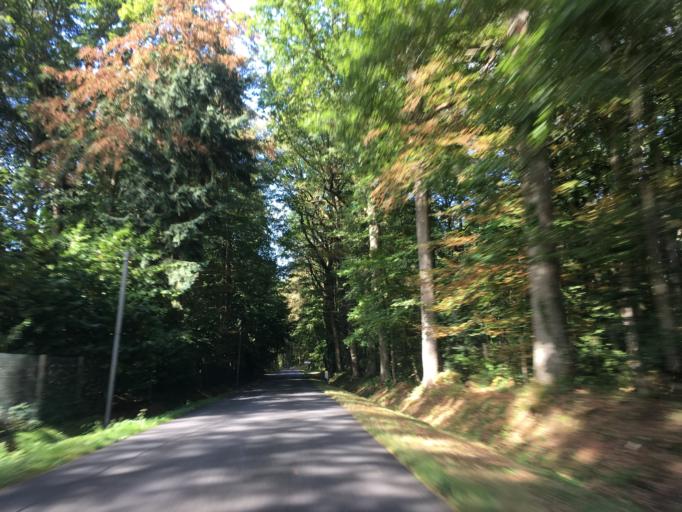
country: FR
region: Ile-de-France
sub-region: Departement des Yvelines
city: Limetz-Villez
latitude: 49.1051
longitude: 1.5285
